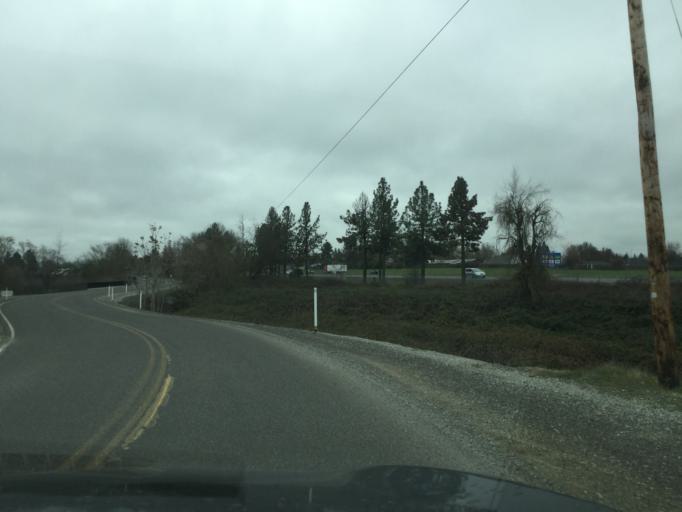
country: US
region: Oregon
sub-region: Jackson County
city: Central Point
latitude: 42.3901
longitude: -122.9183
